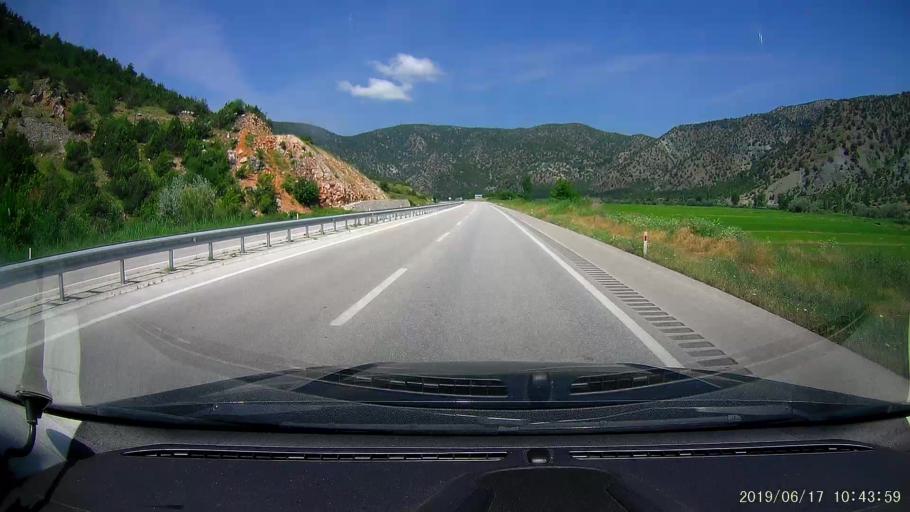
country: TR
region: Corum
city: Kargi
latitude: 41.0707
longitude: 34.5235
